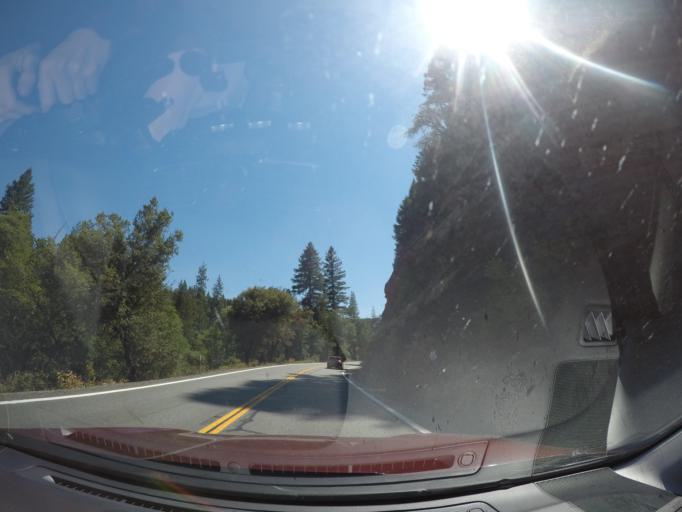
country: US
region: California
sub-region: Shasta County
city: Bella Vista
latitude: 40.7567
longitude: -122.0185
